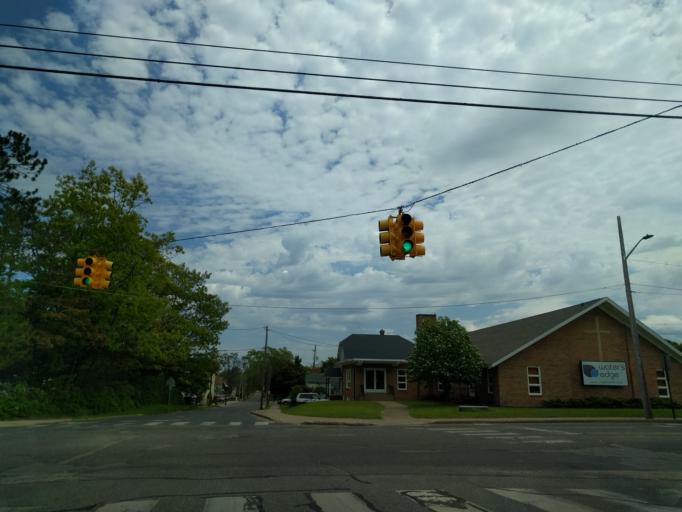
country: US
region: Michigan
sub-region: Marquette County
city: Marquette
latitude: 46.5556
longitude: -87.3966
